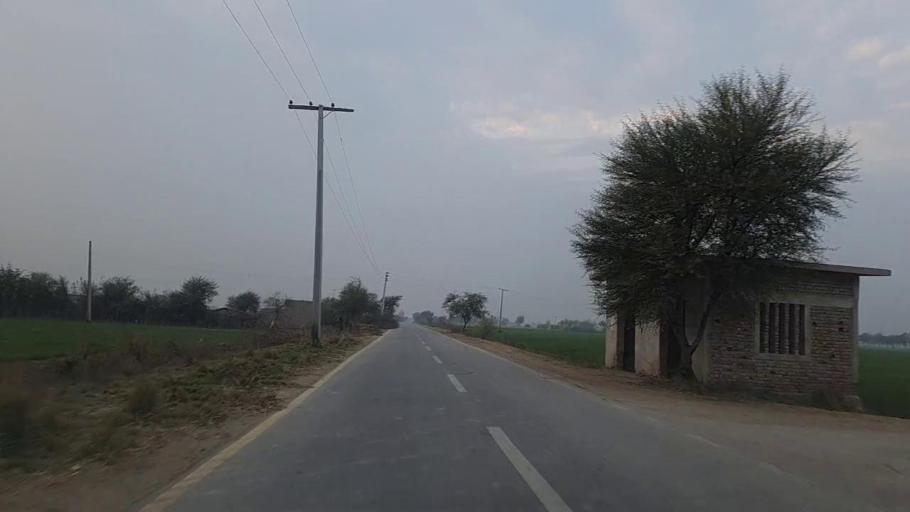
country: PK
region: Sindh
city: Jam Sahib
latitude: 26.3148
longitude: 68.5748
